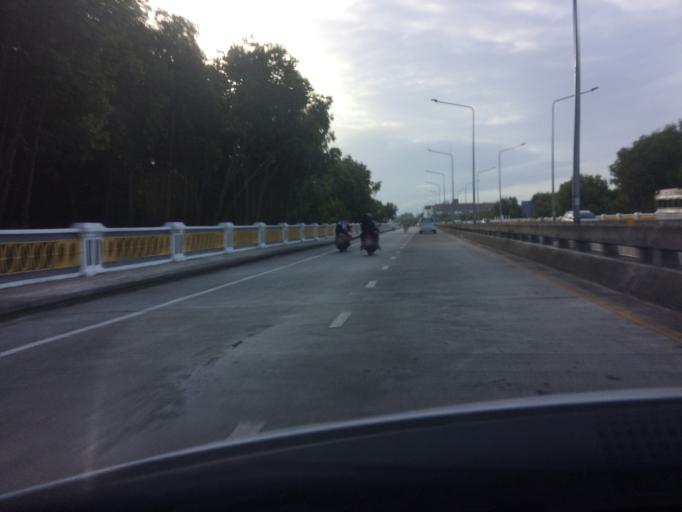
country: TH
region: Phuket
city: Ban Talat Nua
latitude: 7.8689
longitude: 98.3854
